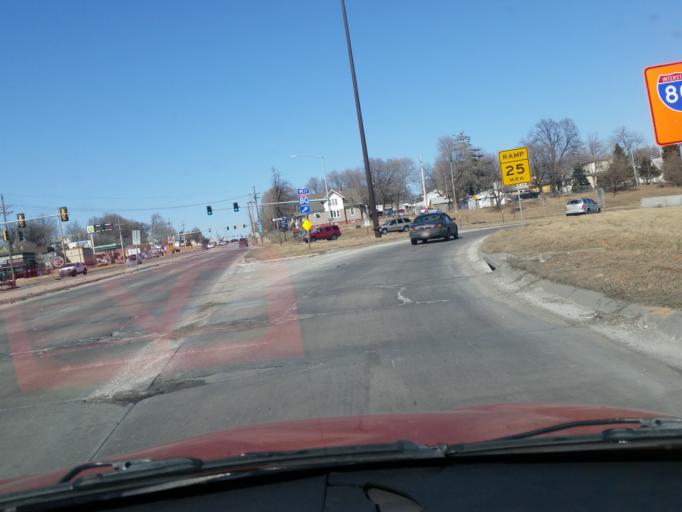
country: US
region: Nebraska
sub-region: Douglas County
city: Omaha
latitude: 41.2301
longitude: -95.9332
